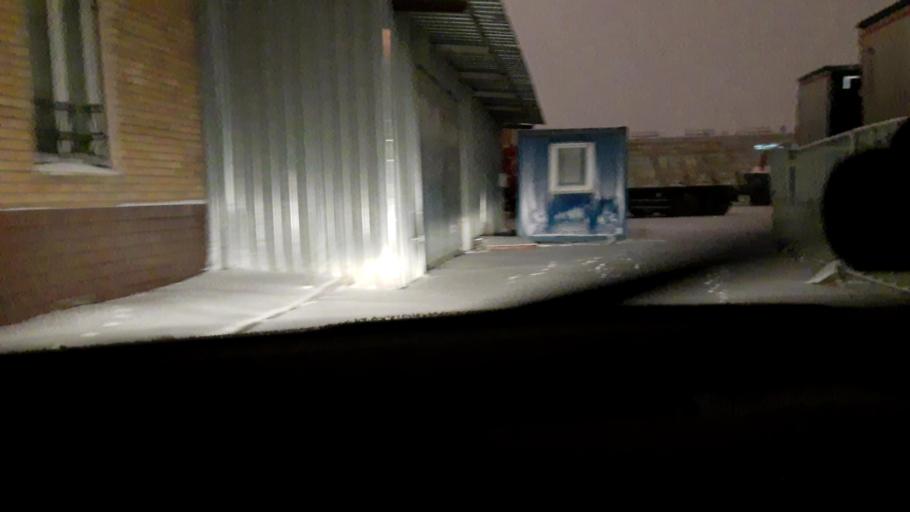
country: RU
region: Moscow
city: Mikhalkovo
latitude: 55.6699
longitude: 37.4365
